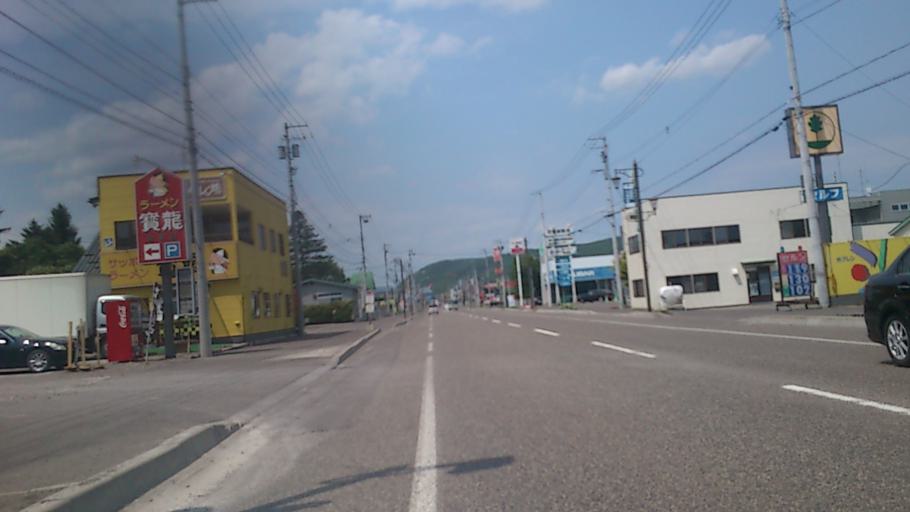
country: JP
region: Hokkaido
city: Otofuke
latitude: 43.2344
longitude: 143.5463
